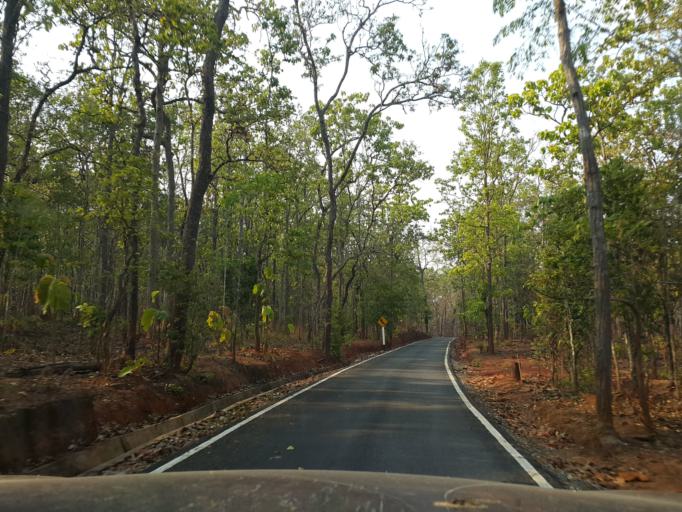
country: TH
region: Lamphun
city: Li
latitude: 17.6371
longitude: 98.8807
